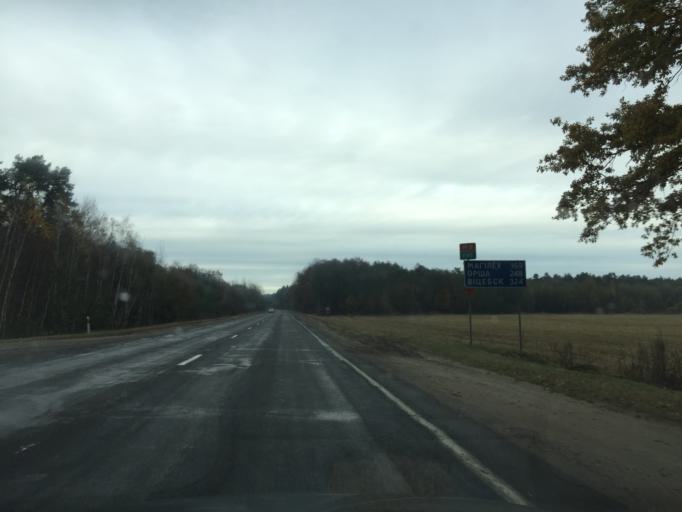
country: BY
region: Gomel
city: Gomel
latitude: 52.3953
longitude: 30.8287
